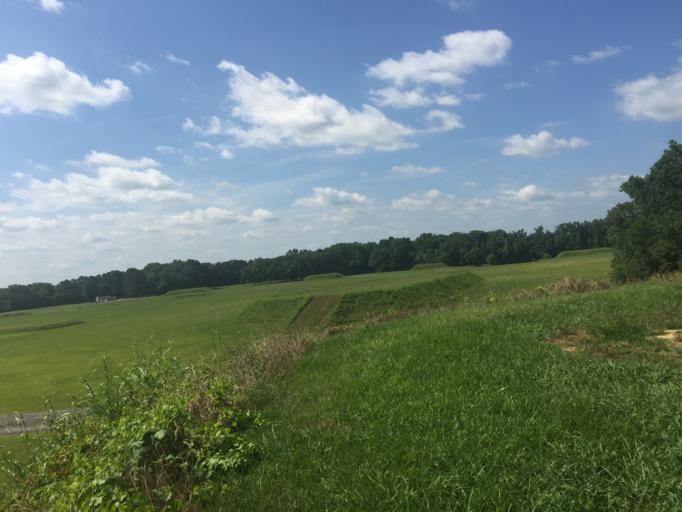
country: US
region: Alabama
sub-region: Hale County
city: Moundville
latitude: 33.0078
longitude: -87.6312
